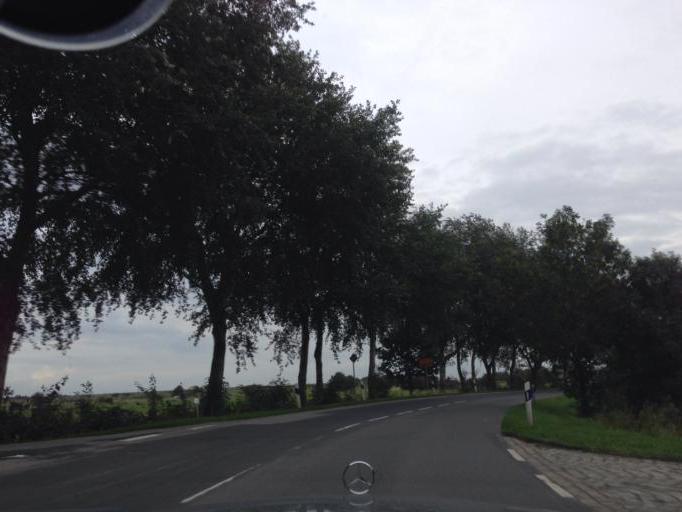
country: DE
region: Schleswig-Holstein
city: Wyk auf Fohr
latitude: 54.6962
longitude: 8.5588
